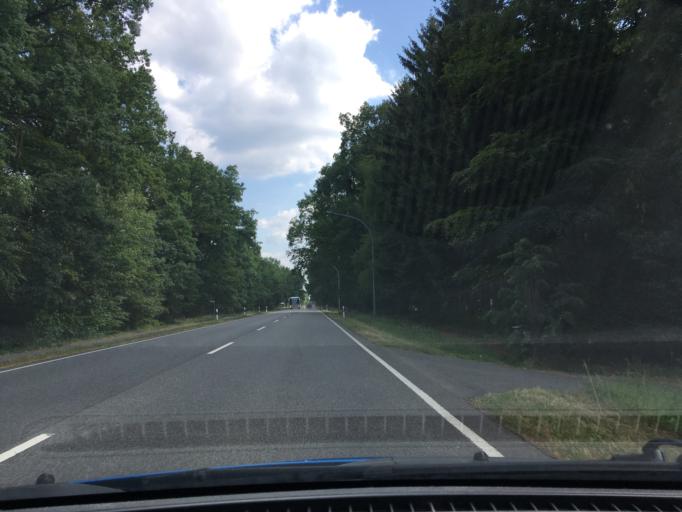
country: DE
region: Lower Saxony
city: Handeloh
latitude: 53.1957
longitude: 9.8290
